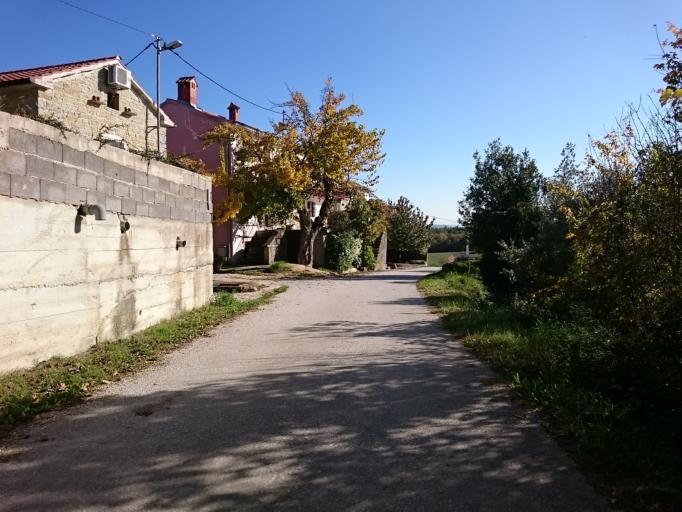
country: HR
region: Istarska
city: Buje
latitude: 45.4361
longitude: 13.7346
